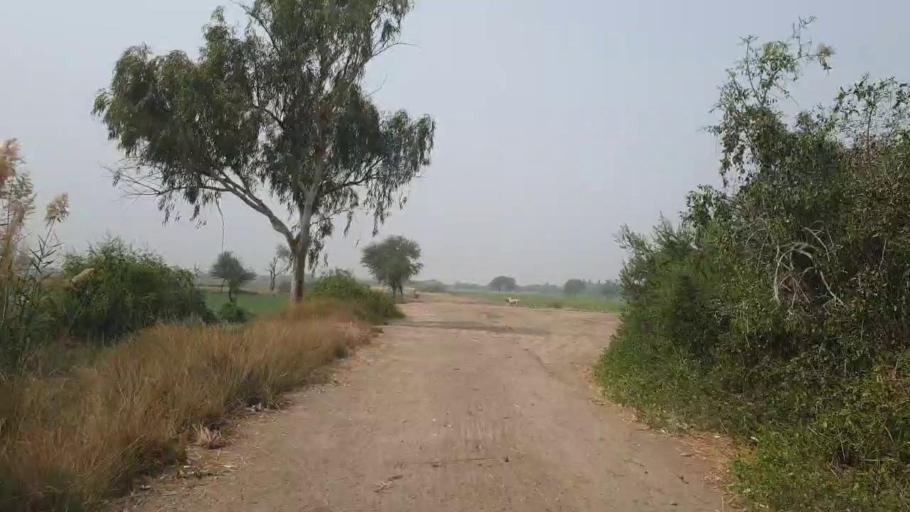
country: PK
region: Sindh
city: Kario
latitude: 24.6604
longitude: 68.6586
